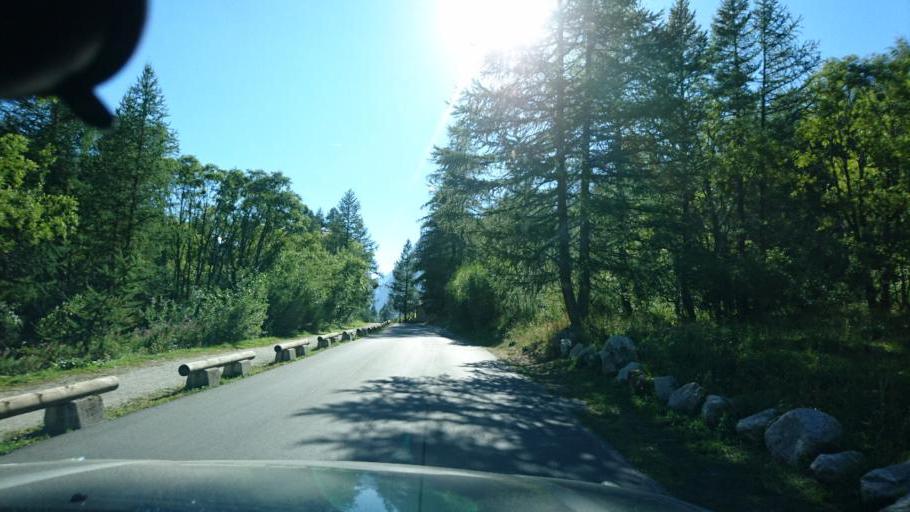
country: IT
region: Aosta Valley
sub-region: Valle d'Aosta
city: Courmayeur
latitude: 45.8352
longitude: 6.9969
